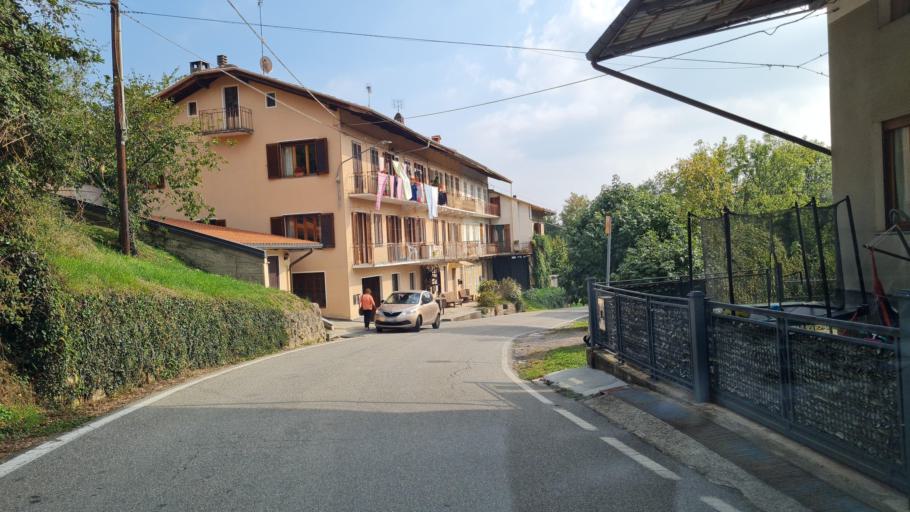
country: IT
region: Piedmont
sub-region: Provincia di Biella
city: Mezzana Mortigliengo
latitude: 45.6264
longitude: 8.1917
